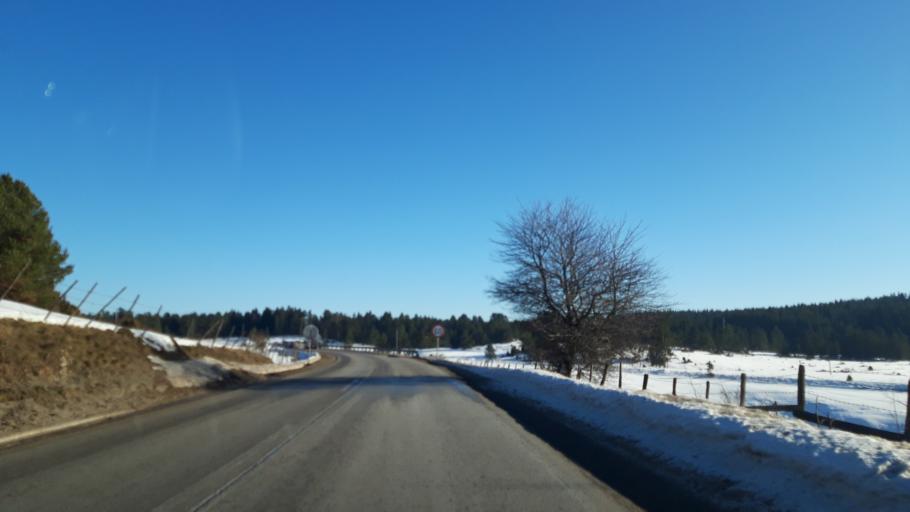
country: BA
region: Republika Srpska
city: Sokolac
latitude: 43.9202
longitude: 18.6856
